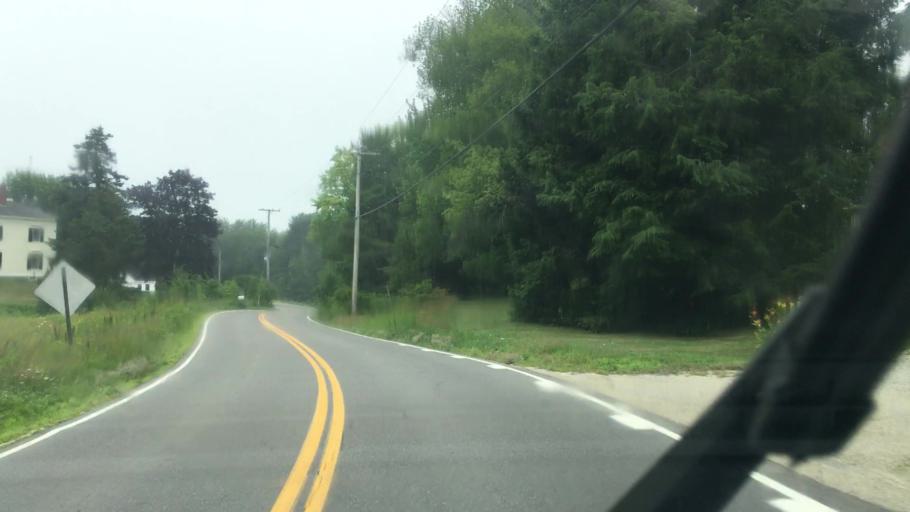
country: US
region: Maine
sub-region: Lincoln County
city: Wiscasset
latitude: 43.9875
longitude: -69.6435
